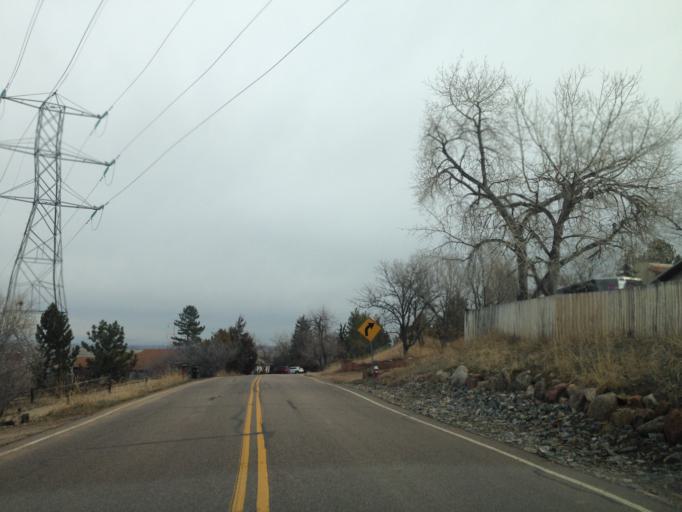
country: US
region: Colorado
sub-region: Boulder County
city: Gunbarrel
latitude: 40.0075
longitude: -105.1988
